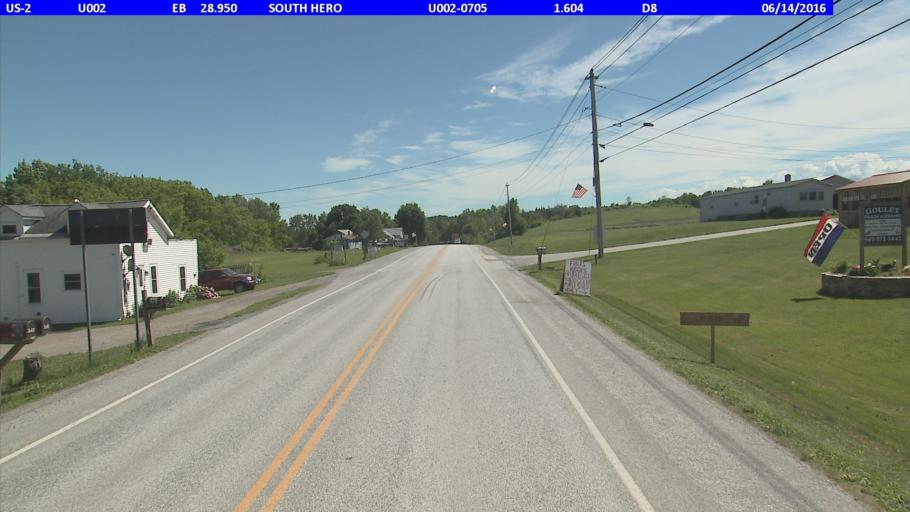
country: US
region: New York
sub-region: Clinton County
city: Cumberland Head
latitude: 44.6580
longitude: -73.3214
